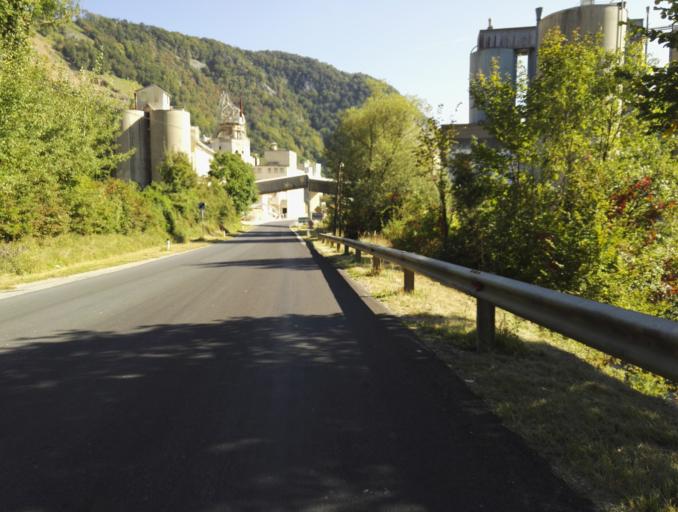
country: AT
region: Styria
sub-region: Politischer Bezirk Graz-Umgebung
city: Peggau
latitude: 47.2177
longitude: 15.3388
